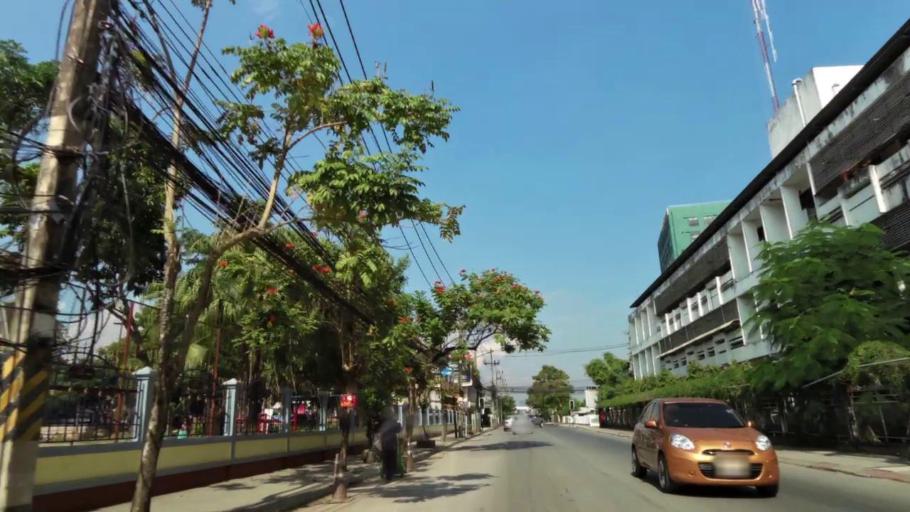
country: TH
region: Chiang Rai
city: Chiang Rai
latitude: 19.9014
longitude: 99.8281
